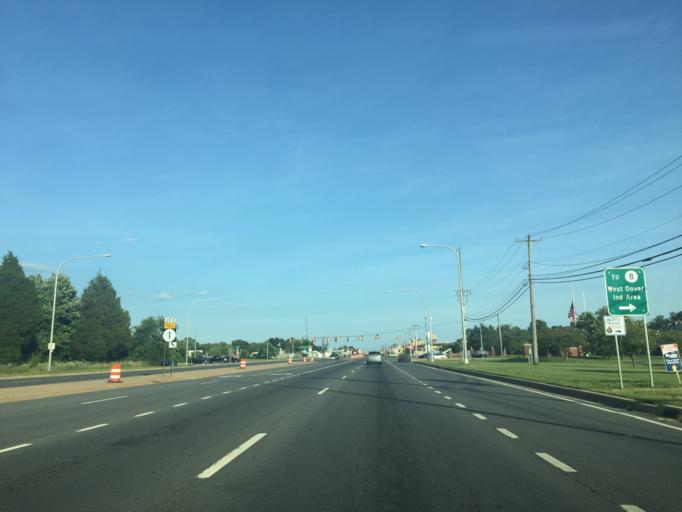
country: US
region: Delaware
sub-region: Kent County
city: Cheswold
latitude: 39.2010
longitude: -75.5574
